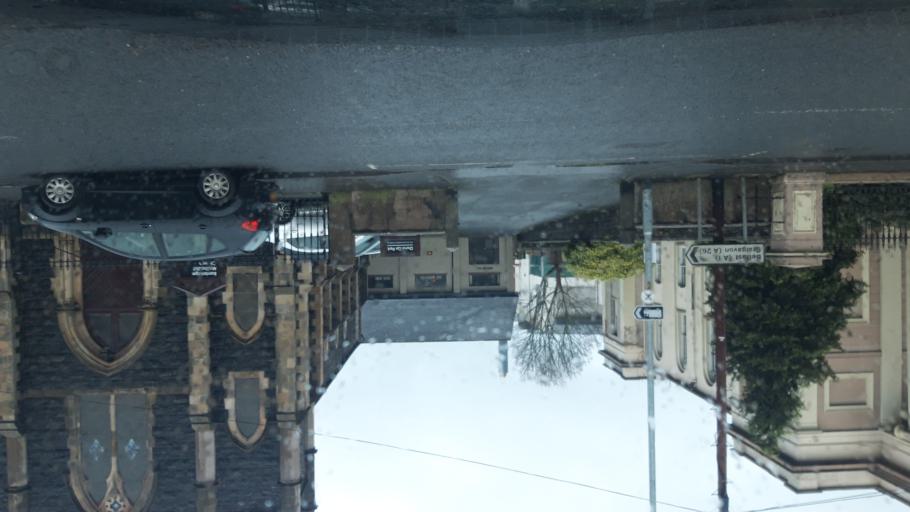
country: GB
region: Northern Ireland
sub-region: Banbridge District
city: Banbridge
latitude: 54.3512
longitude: -6.2696
